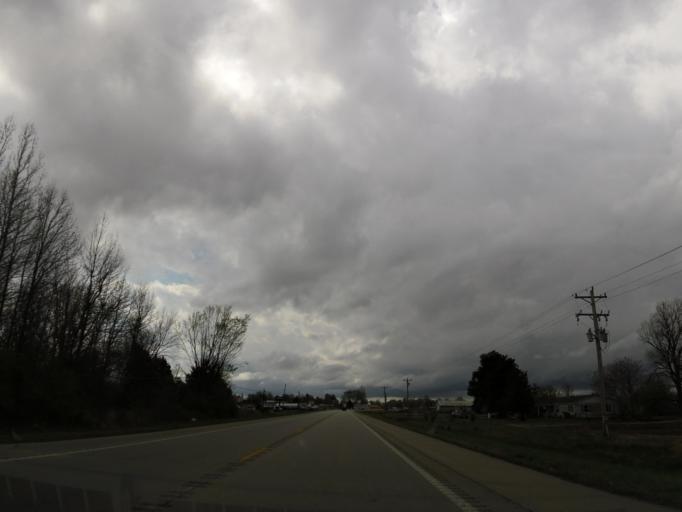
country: US
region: Arkansas
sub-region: Clay County
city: Corning
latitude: 36.5528
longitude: -90.5212
